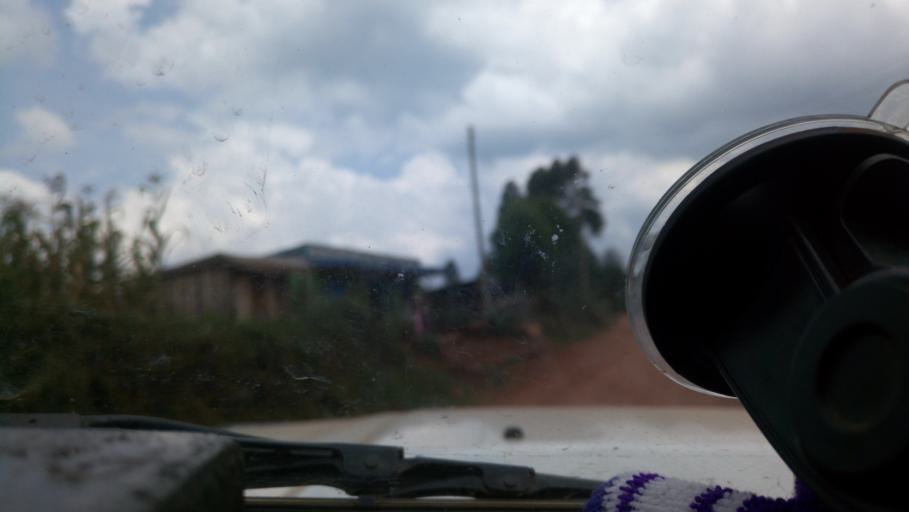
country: KE
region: Kericho
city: Litein
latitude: -0.6008
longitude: 35.1829
